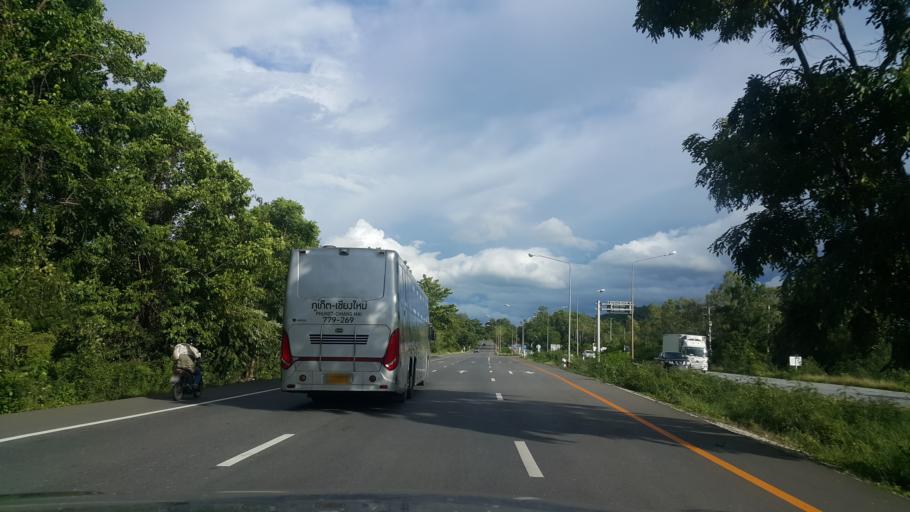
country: TH
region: Tak
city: Ban Tak
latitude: 16.9778
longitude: 99.1258
